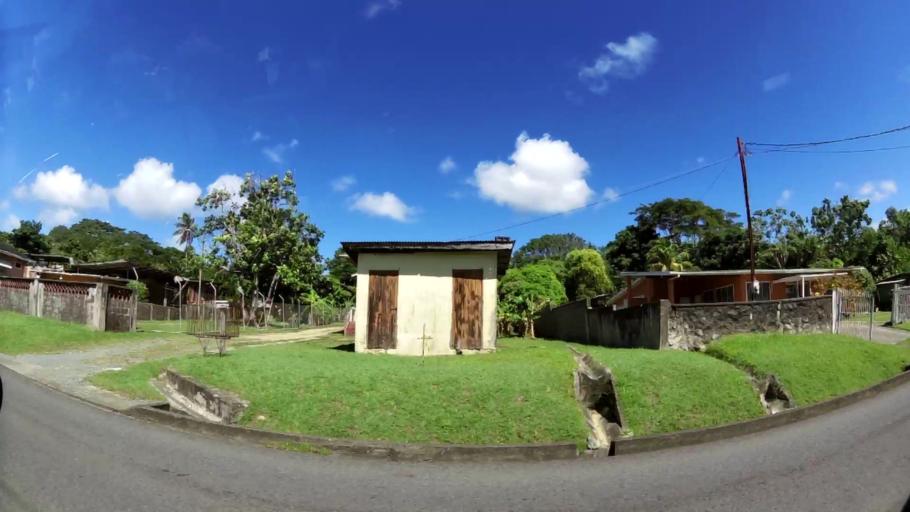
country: TT
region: Tobago
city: Scarborough
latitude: 11.1689
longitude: -60.7771
